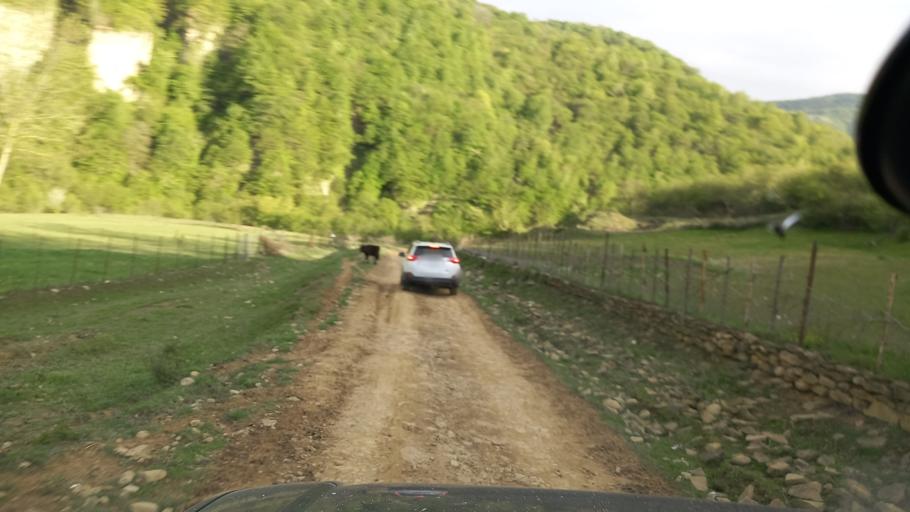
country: RU
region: Dagestan
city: Khuchni
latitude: 41.9462
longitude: 47.8344
